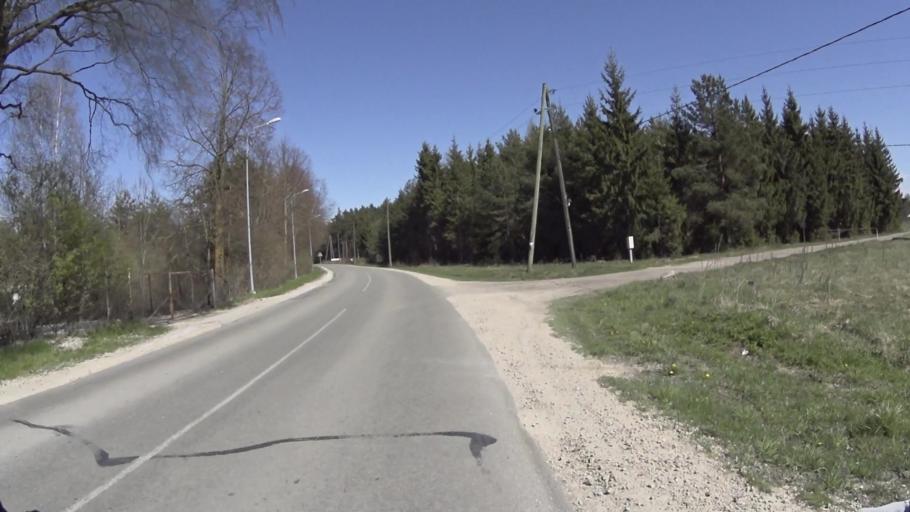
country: LV
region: Babite
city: Pinki
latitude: 56.9777
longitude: 23.9717
